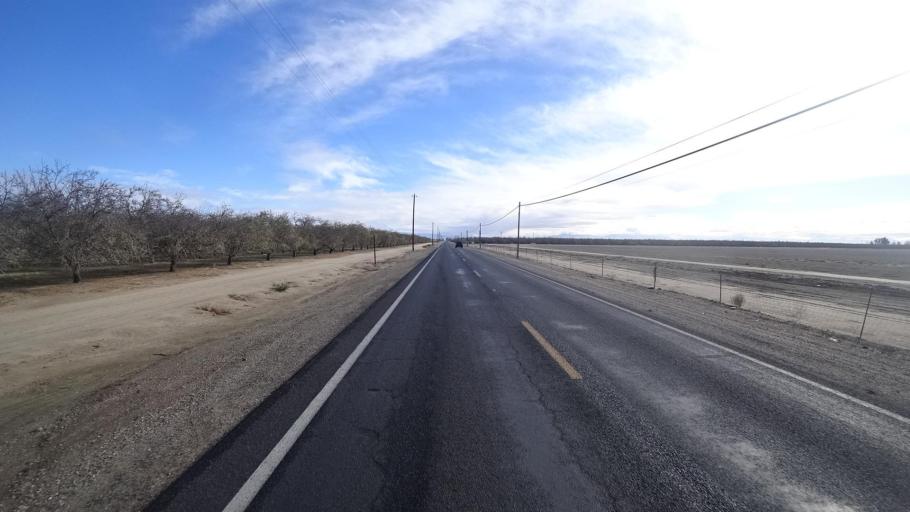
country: US
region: California
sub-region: Kern County
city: Rosedale
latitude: 35.3835
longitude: -119.2379
